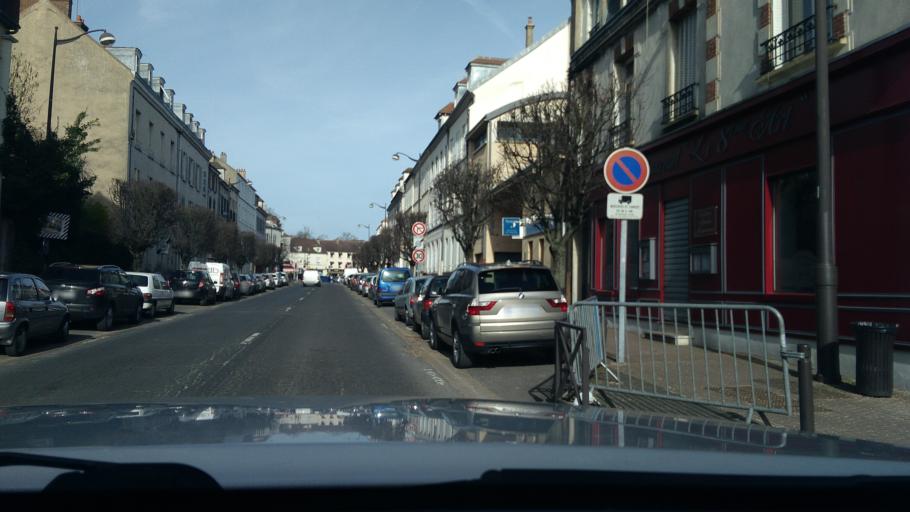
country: FR
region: Ile-de-France
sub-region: Departement de Seine-et-Marne
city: Melun
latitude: 48.5379
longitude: 2.6612
